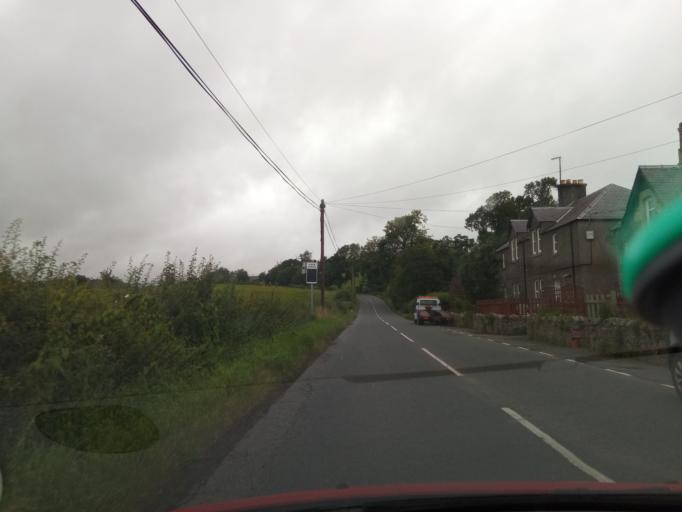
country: GB
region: Scotland
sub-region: The Scottish Borders
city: Kelso
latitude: 55.6279
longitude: -2.5045
